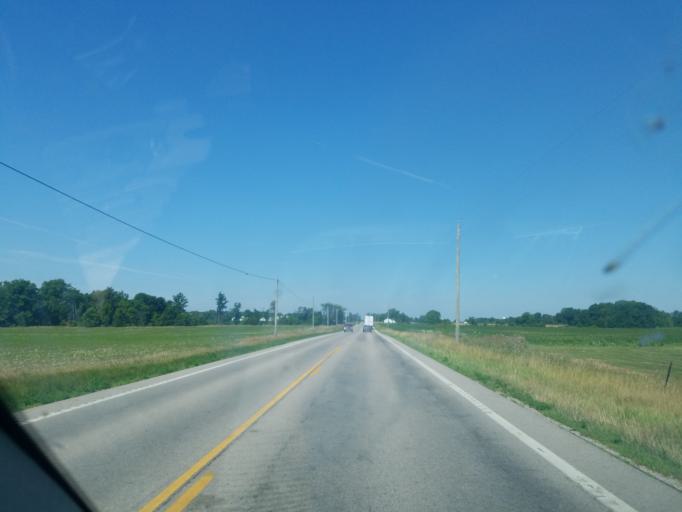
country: US
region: Ohio
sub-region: Shelby County
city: Jackson Center
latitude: 40.4393
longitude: -84.0088
